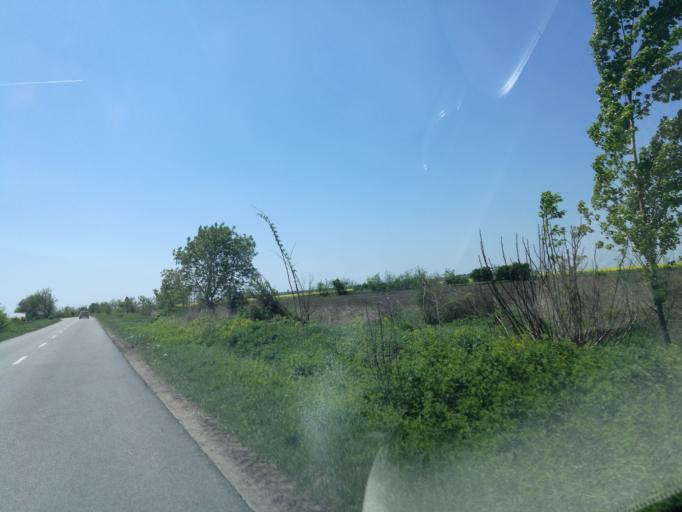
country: RO
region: Prahova
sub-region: Comuna Gherghita
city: Gherghita
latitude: 44.7863
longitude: 26.2626
